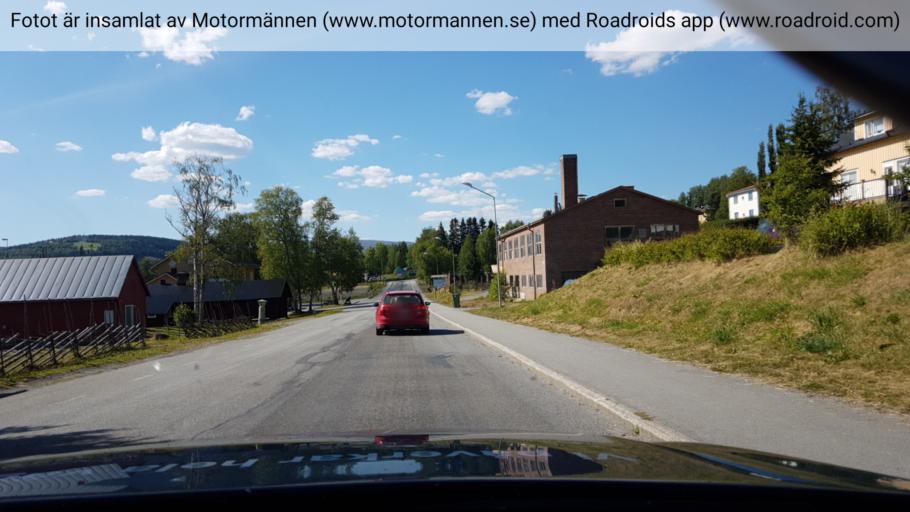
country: SE
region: Jaemtland
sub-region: Are Kommun
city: Are
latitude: 63.3140
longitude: 13.2406
